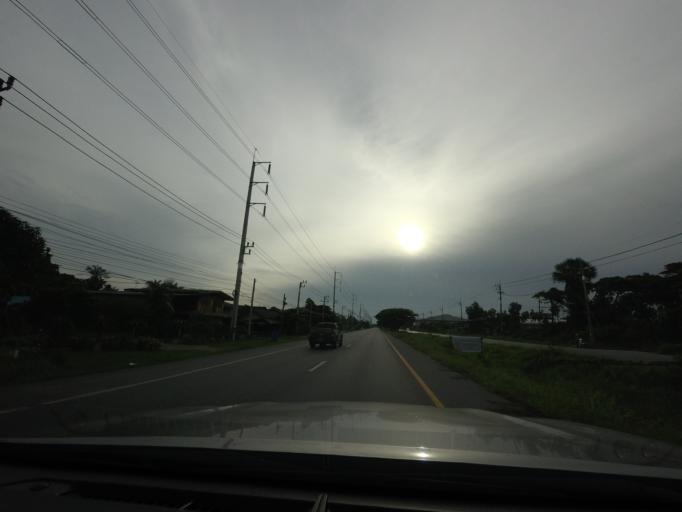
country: TH
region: Nakhon Si Thammarat
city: Hua Sai
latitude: 8.0487
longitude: 100.2654
